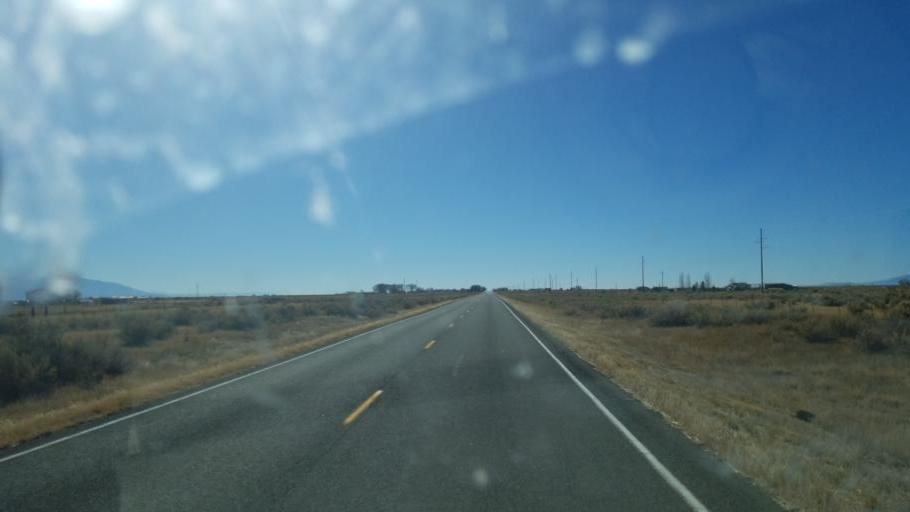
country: US
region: Colorado
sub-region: Saguache County
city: Saguache
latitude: 38.0313
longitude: -105.9121
